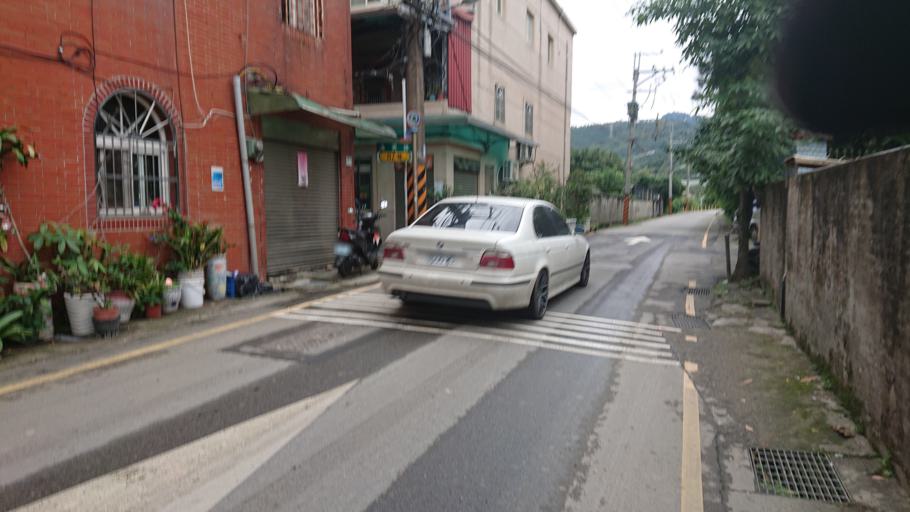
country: TW
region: Taipei
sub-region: Taipei
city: Banqiao
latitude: 24.9621
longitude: 121.4418
